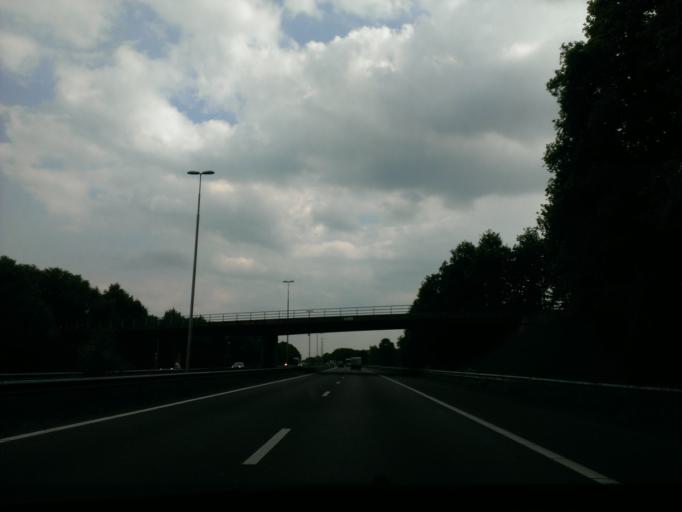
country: NL
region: Gelderland
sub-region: Gemeente Heerde
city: Heerde
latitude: 52.3880
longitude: 6.0154
